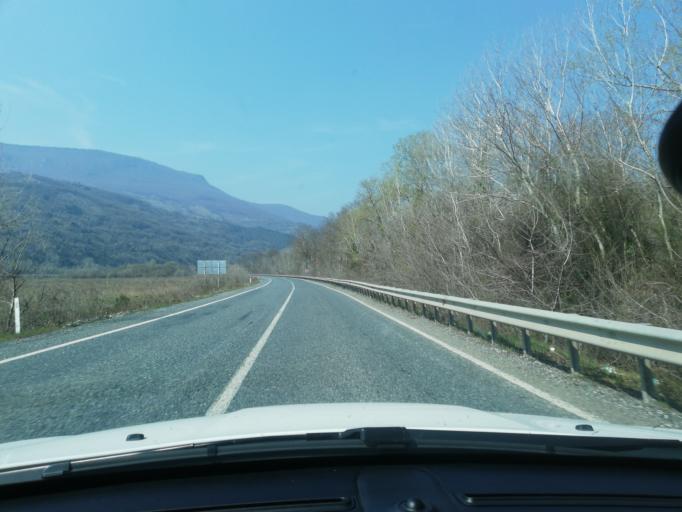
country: TR
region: Karabuk
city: Yenice
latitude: 41.2150
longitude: 32.2800
